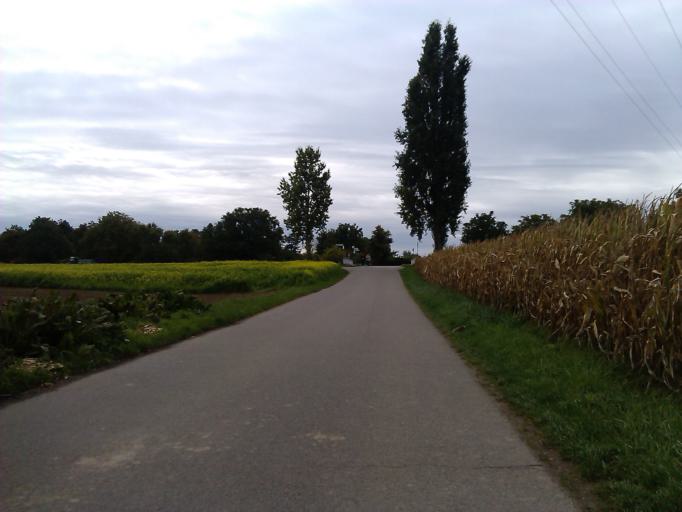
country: DE
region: Baden-Wuerttemberg
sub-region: Karlsruhe Region
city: Weinheim
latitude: 49.5636
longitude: 8.6482
